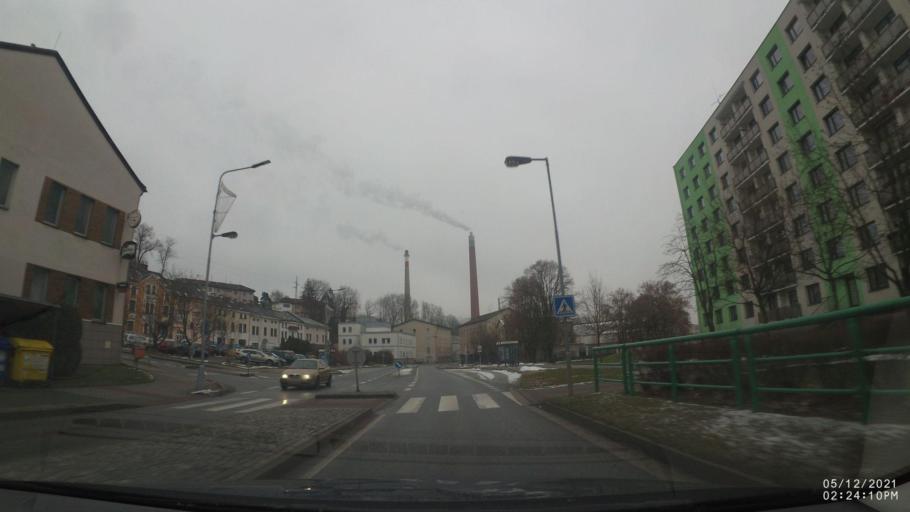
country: CZ
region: Kralovehradecky
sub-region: Okres Nachod
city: Nachod
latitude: 50.4222
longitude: 16.1671
